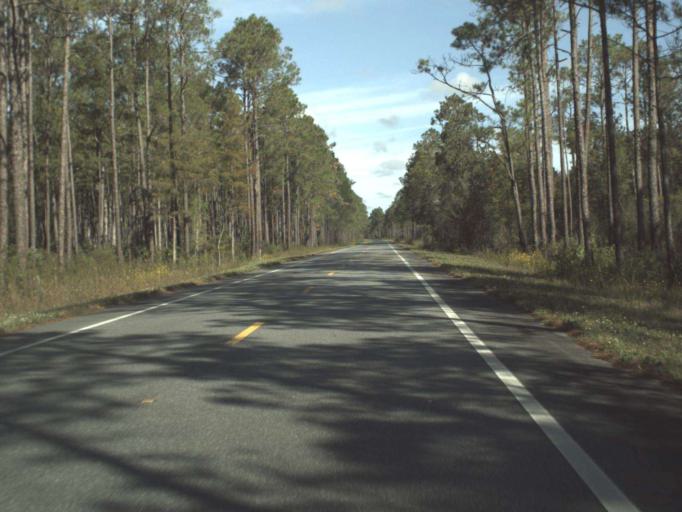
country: US
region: Florida
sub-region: Franklin County
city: Apalachicola
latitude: 29.9681
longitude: -84.9755
